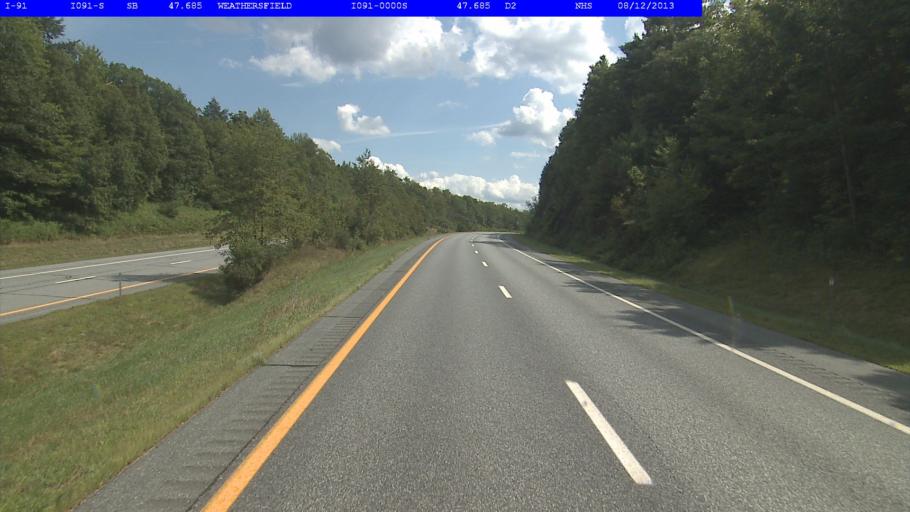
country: US
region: New Hampshire
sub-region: Sullivan County
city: Claremont
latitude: 43.3508
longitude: -72.4203
